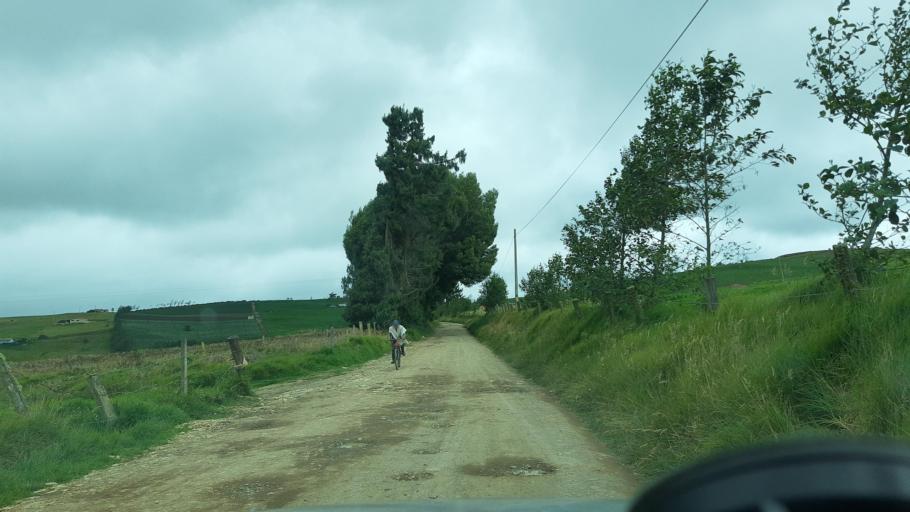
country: CO
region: Boyaca
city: Samaca
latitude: 5.4945
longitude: -73.4533
